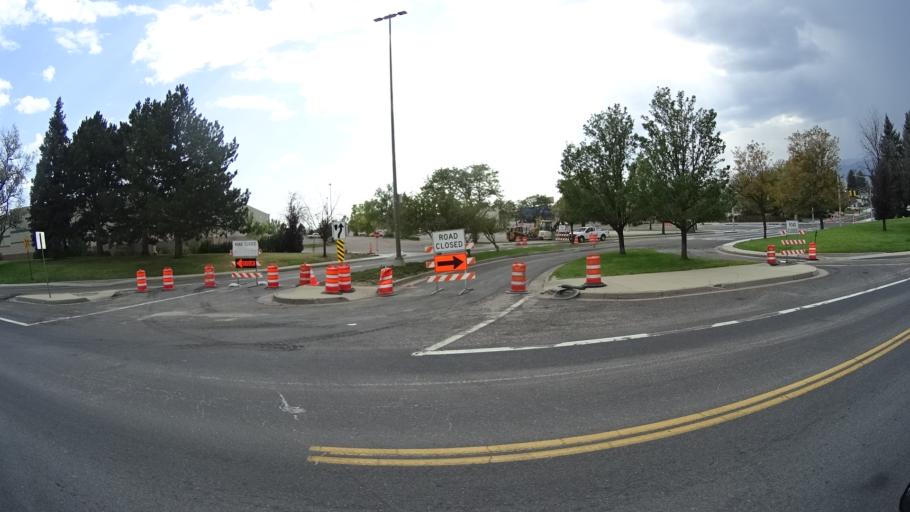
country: US
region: Colorado
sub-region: El Paso County
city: Colorado Springs
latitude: 38.8425
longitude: -104.7655
